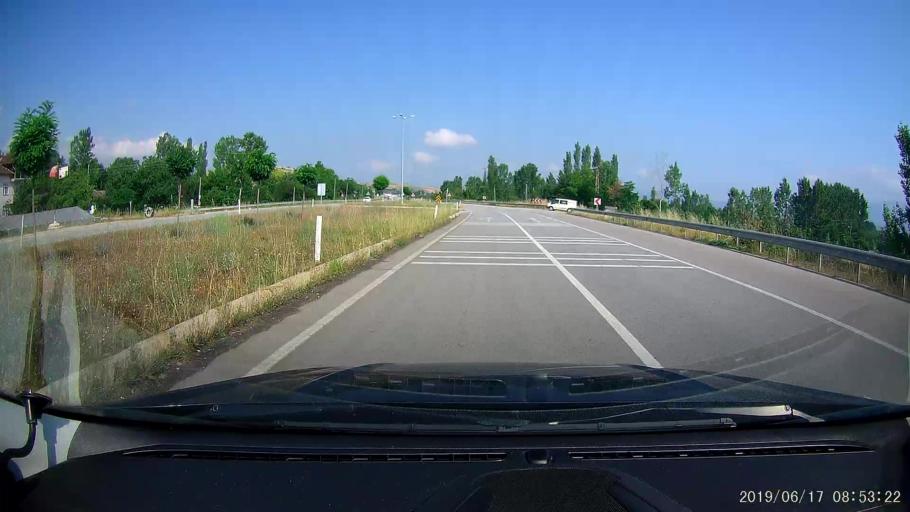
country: TR
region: Tokat
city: Erbaa
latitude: 40.7093
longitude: 36.4825
